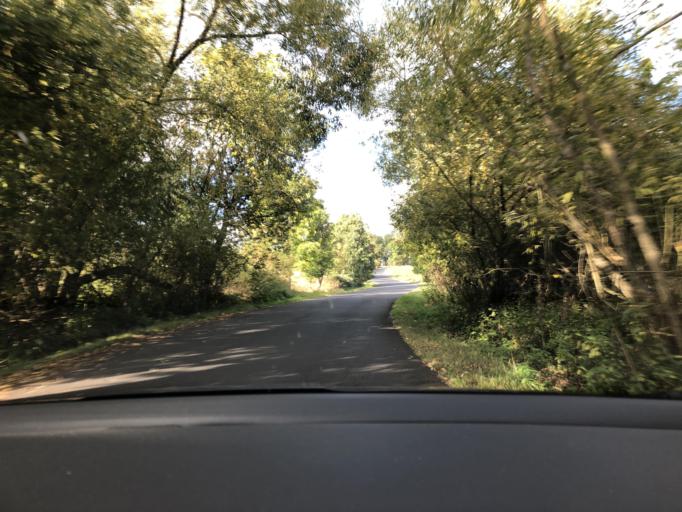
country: CZ
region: Ustecky
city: Zitenice
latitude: 50.6080
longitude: 14.1637
